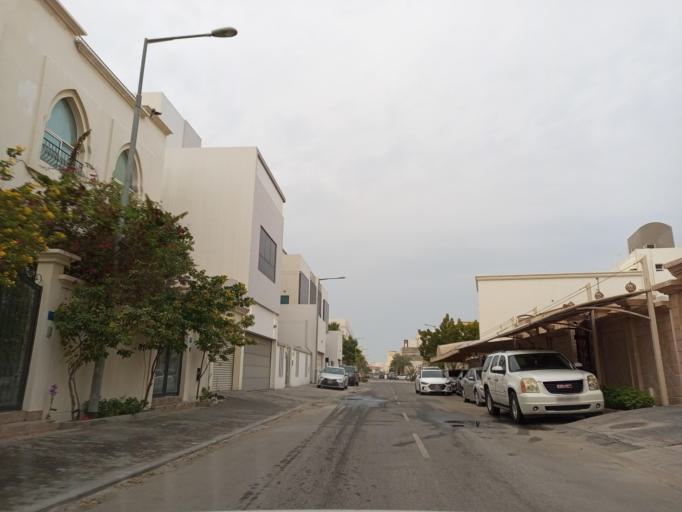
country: BH
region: Muharraq
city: Al Hadd
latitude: 26.2439
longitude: 50.6421
